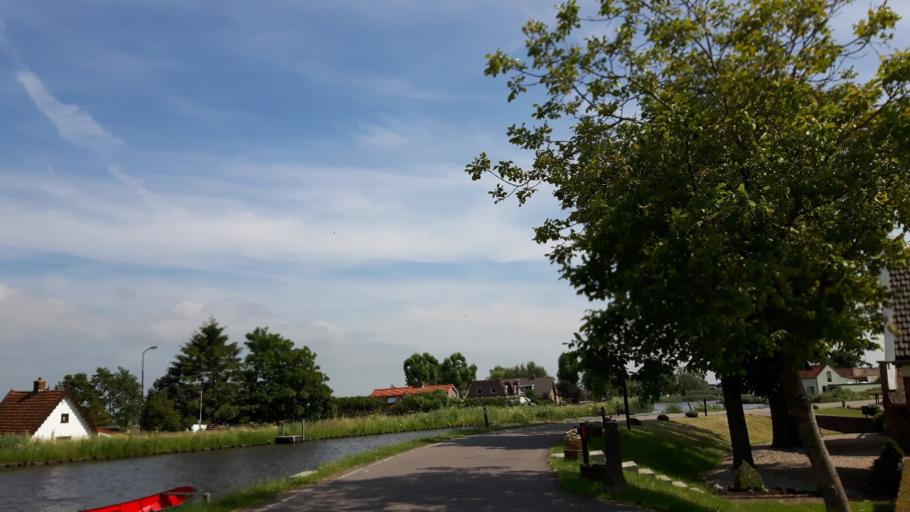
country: NL
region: North Holland
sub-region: Gemeente Uithoorn
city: Uithoorn
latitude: 52.2073
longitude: 4.8142
